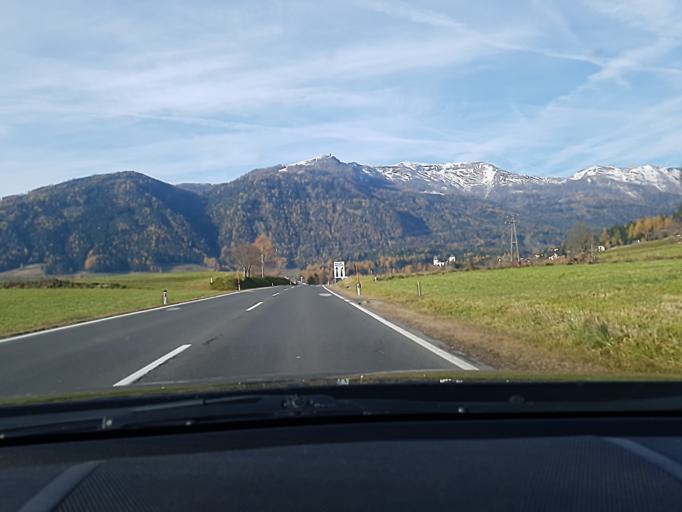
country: AT
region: Salzburg
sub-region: Politischer Bezirk Tamsweg
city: Mauterndorf
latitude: 47.1372
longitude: 13.6955
